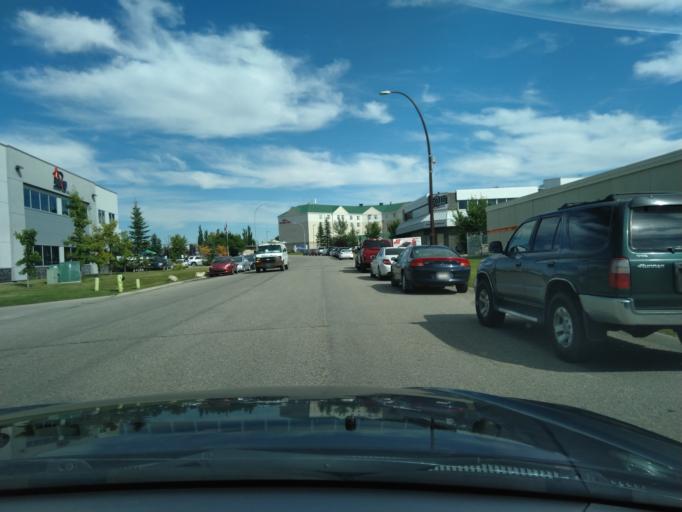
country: CA
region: Alberta
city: Calgary
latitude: 51.0940
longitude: -114.0075
